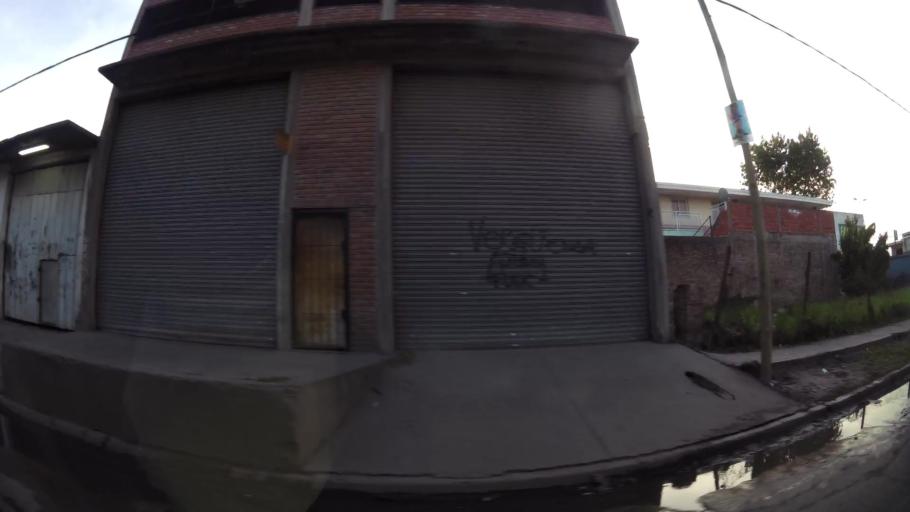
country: AR
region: Buenos Aires
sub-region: Partido de Almirante Brown
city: Adrogue
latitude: -34.7743
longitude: -58.3249
